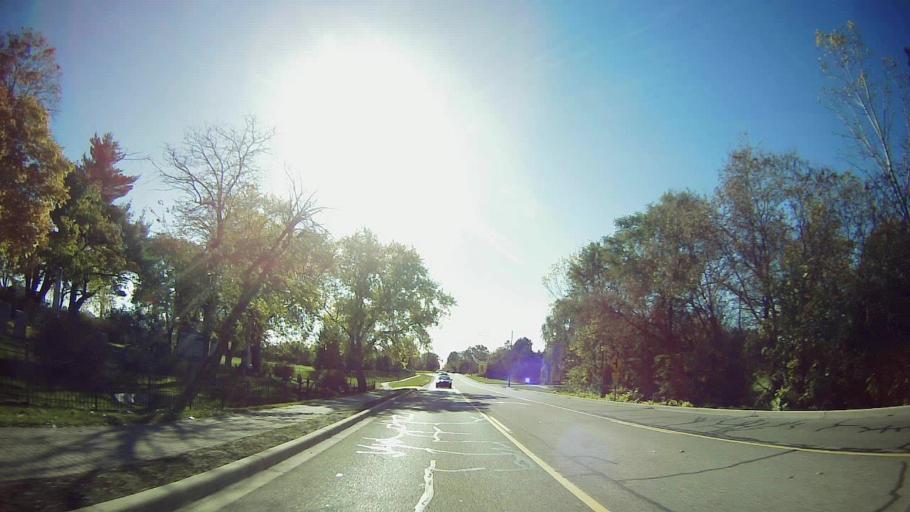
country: US
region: Michigan
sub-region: Oakland County
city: Farmington Hills
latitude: 42.5179
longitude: -83.3792
